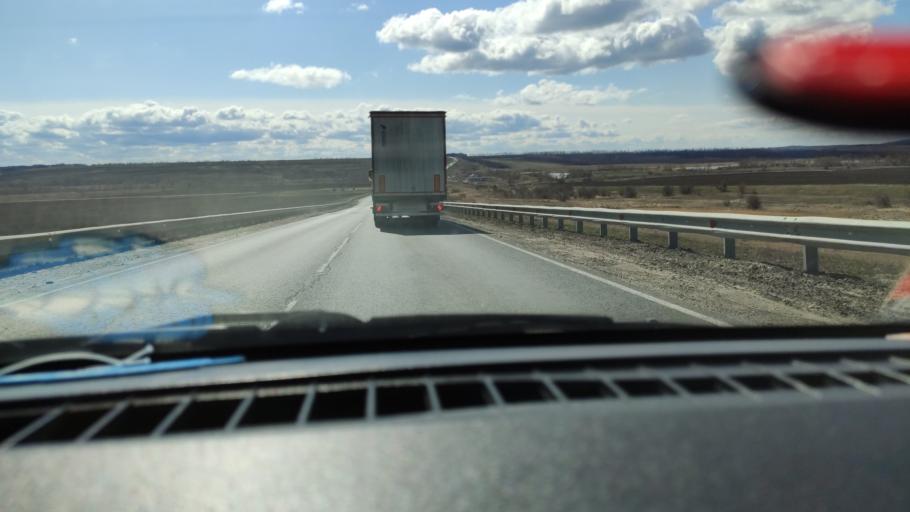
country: RU
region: Saratov
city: Dukhovnitskoye
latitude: 52.7457
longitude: 48.2517
